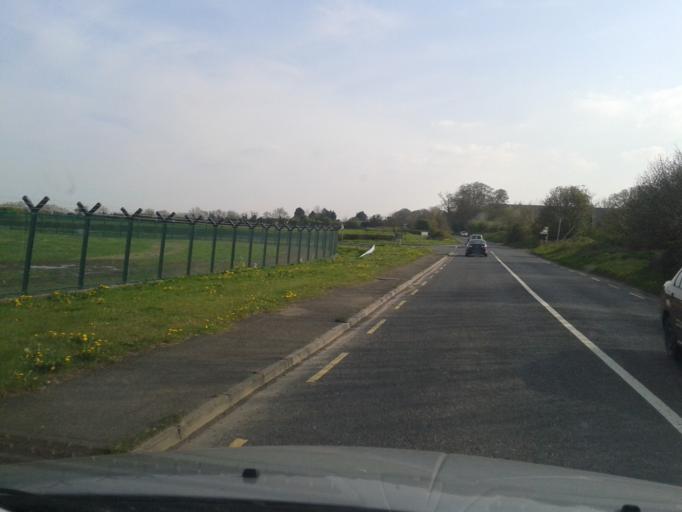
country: IE
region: Leinster
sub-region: Dublin City
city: Finglas
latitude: 53.4231
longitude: -6.3056
